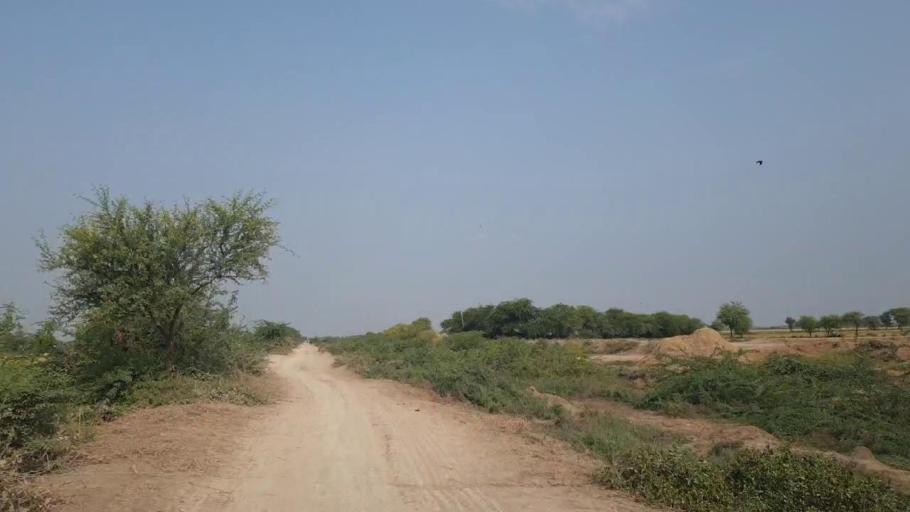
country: PK
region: Sindh
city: Badin
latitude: 24.7337
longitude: 68.7667
